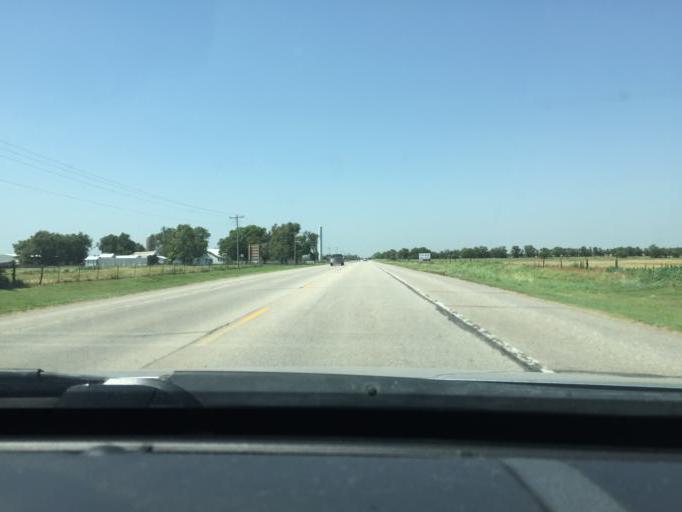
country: US
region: Kansas
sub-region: Reno County
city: Haven
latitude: 37.9485
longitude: -97.8668
